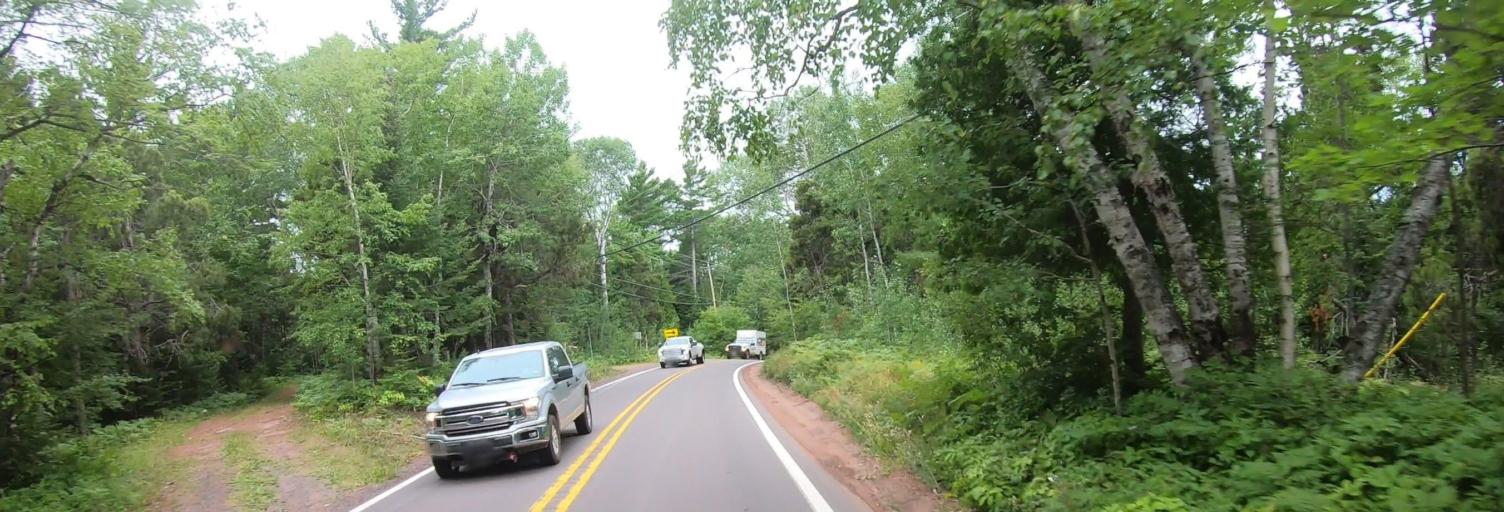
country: US
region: Michigan
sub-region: Keweenaw County
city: Eagle River
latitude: 47.4586
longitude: -88.1251
